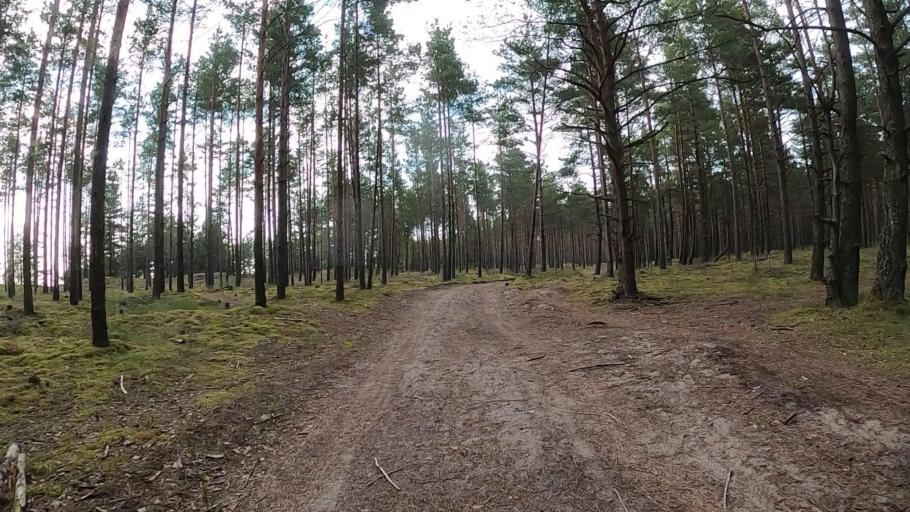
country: LV
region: Carnikava
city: Carnikava
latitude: 57.1471
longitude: 24.2492
